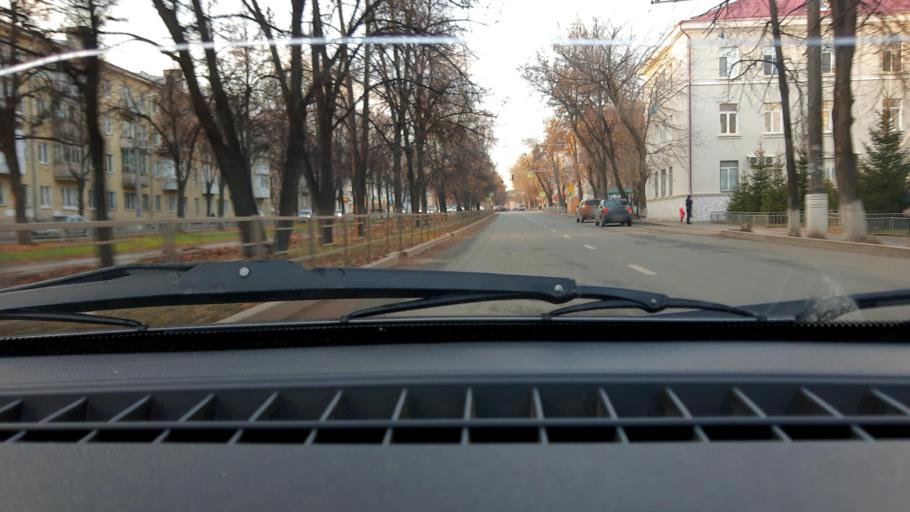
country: RU
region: Bashkortostan
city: Ufa
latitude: 54.8162
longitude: 56.1034
